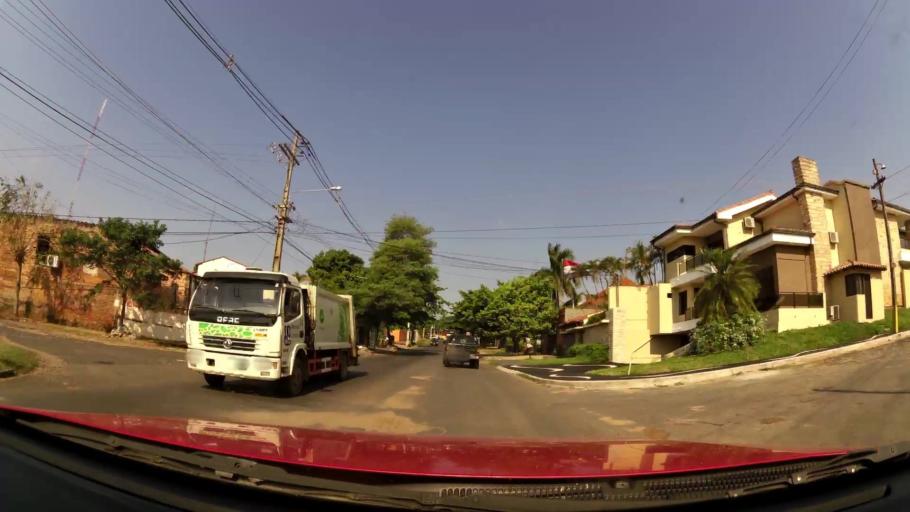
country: PY
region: Asuncion
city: Asuncion
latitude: -25.3175
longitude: -57.6322
